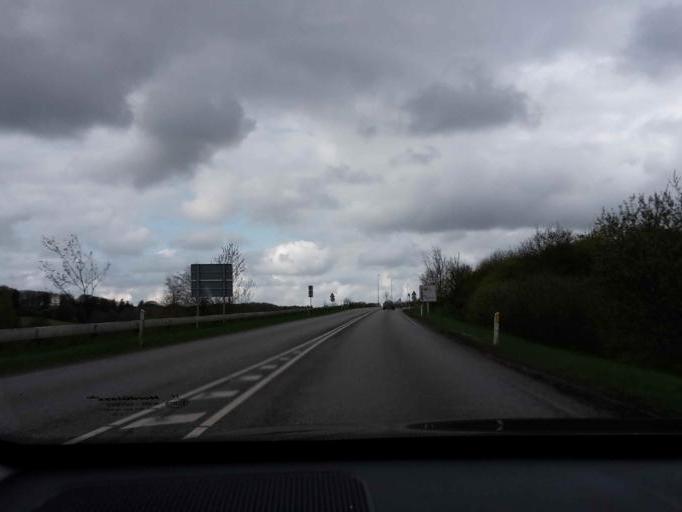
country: DK
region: South Denmark
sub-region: Vejle Kommune
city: Jelling
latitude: 55.7015
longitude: 9.4223
